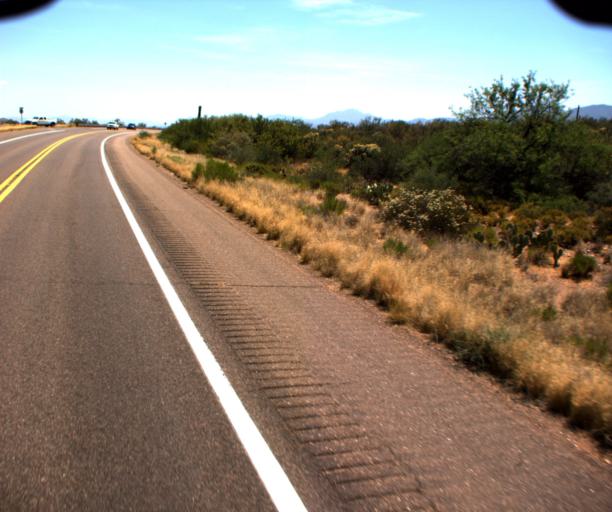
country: US
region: Arizona
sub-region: Gila County
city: Tonto Basin
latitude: 33.9352
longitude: -111.3148
